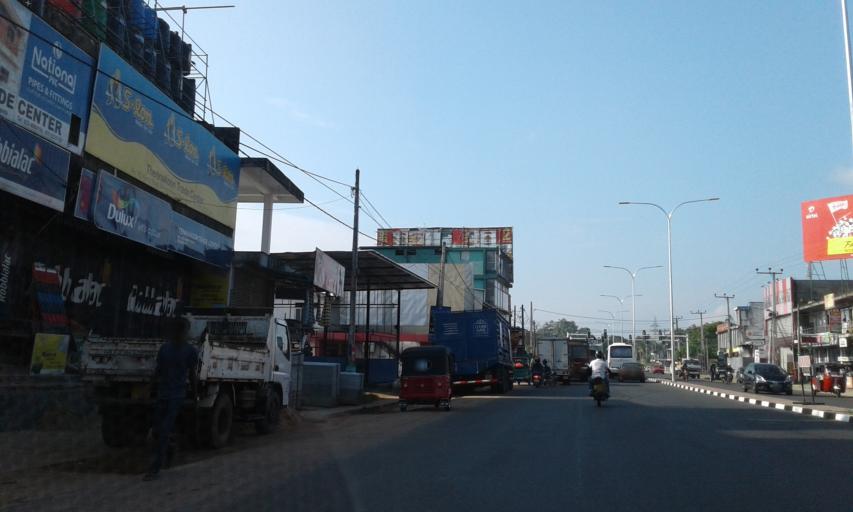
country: LK
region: Western
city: Gampaha
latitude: 7.0678
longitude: 80.0128
